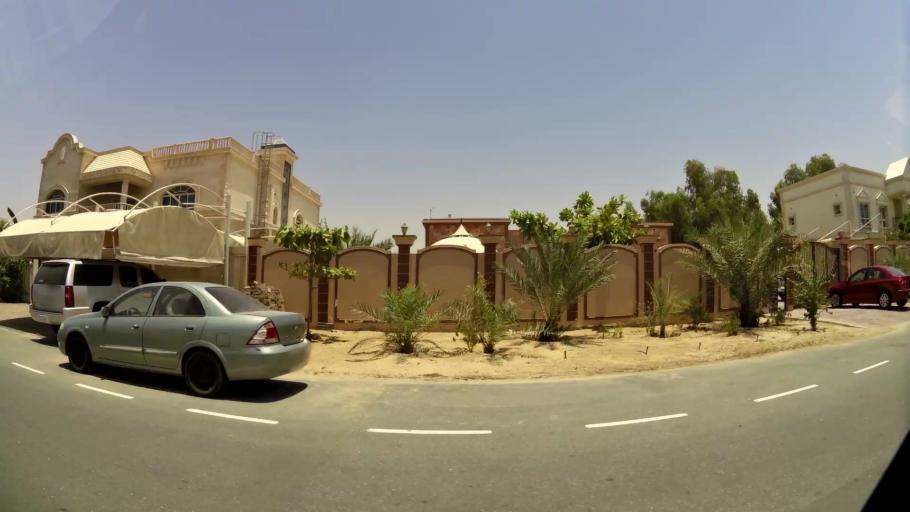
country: AE
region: Dubai
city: Dubai
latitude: 25.0974
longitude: 55.1881
